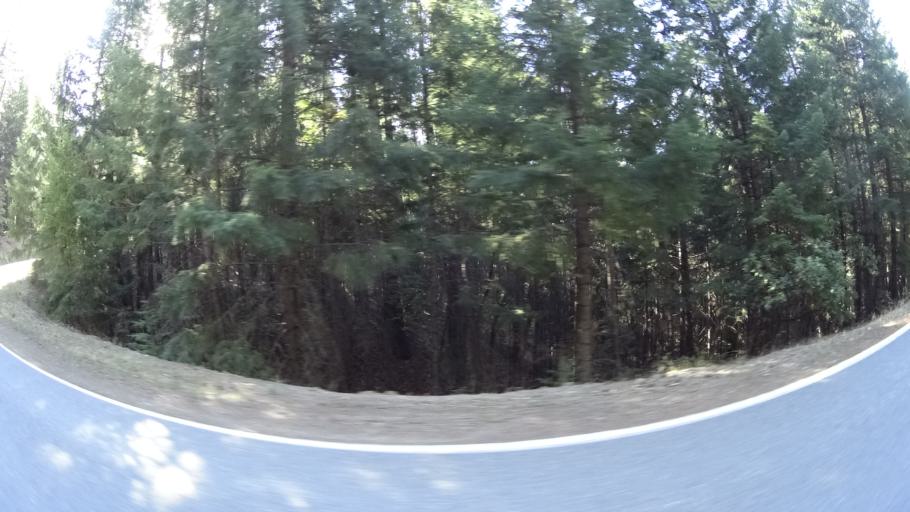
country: US
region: California
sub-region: Trinity County
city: Weaverville
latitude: 41.2094
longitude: -123.0581
